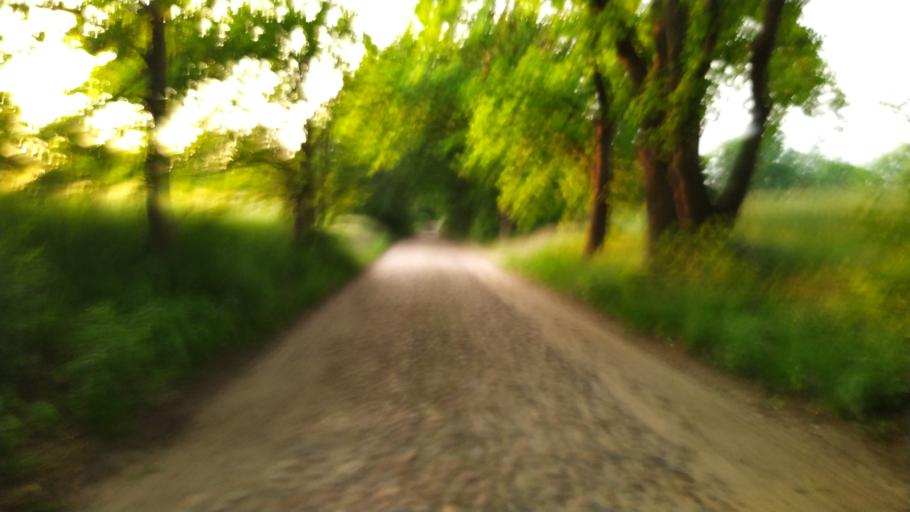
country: DE
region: Lower Saxony
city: Neu Wulmstorf
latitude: 53.4768
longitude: 9.8285
